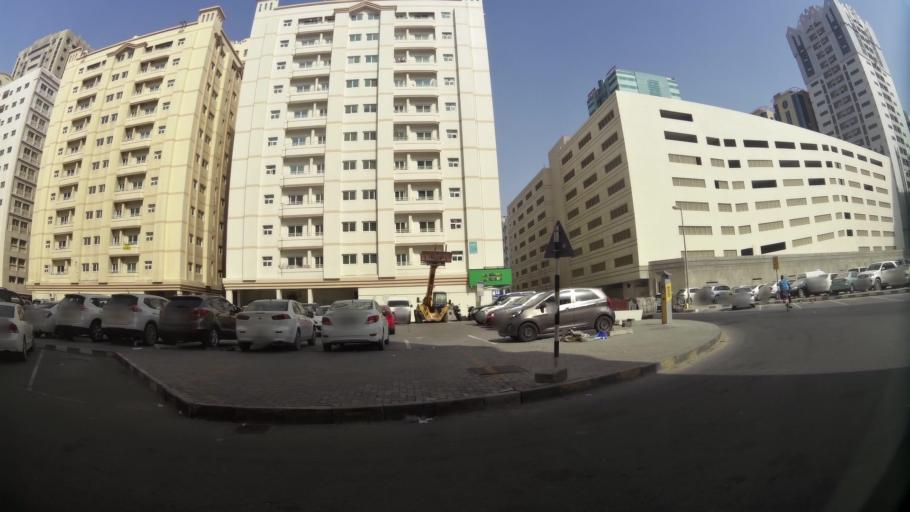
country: AE
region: Ash Shariqah
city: Sharjah
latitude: 25.3429
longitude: 55.3930
